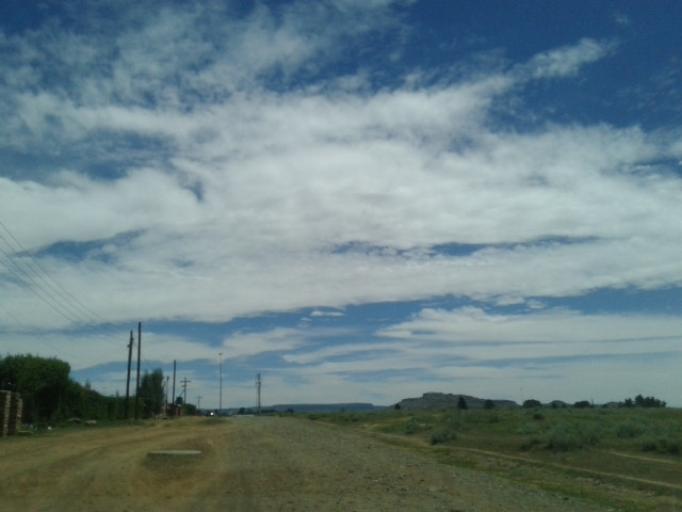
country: LS
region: Maseru
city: Maseru
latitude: -29.2920
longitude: 27.5369
